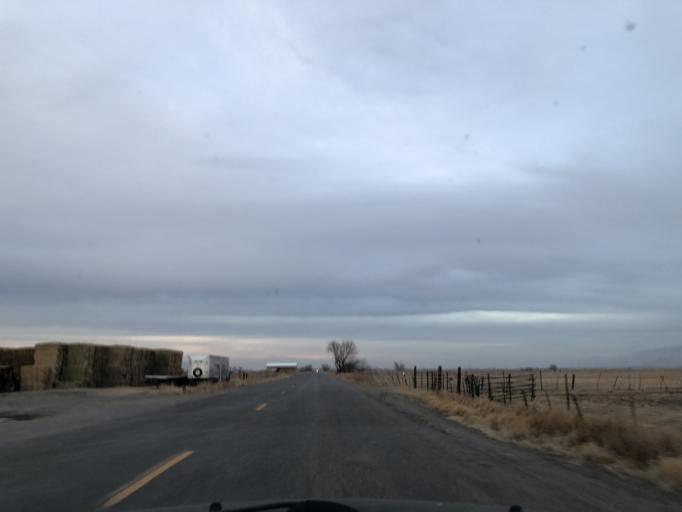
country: US
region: Utah
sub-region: Cache County
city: Benson
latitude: 41.7499
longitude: -111.9116
